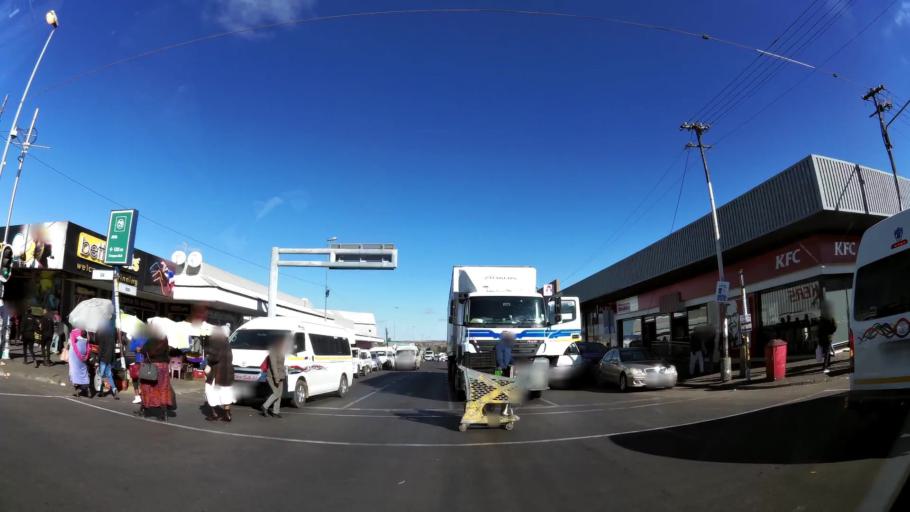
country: ZA
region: Limpopo
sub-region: Capricorn District Municipality
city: Polokwane
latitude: -23.9031
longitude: 29.4481
